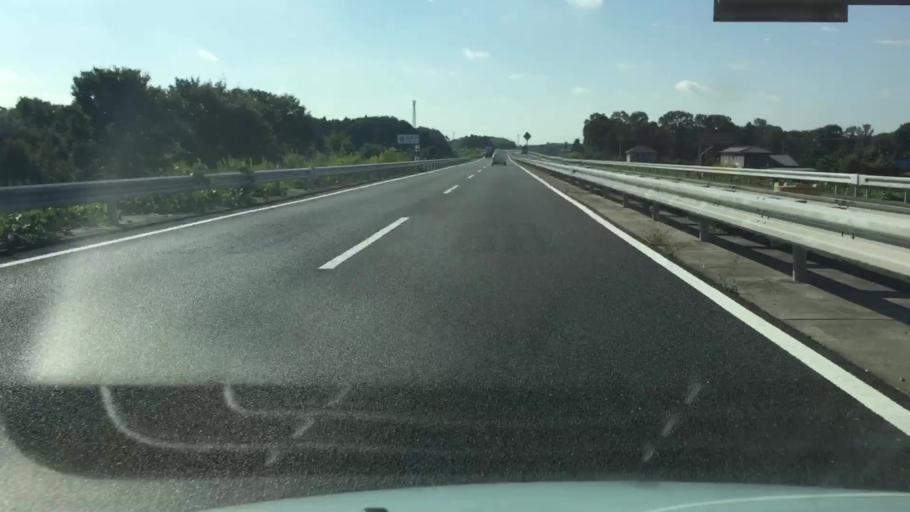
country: JP
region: Tochigi
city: Mooka
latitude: 36.5047
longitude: 139.9882
